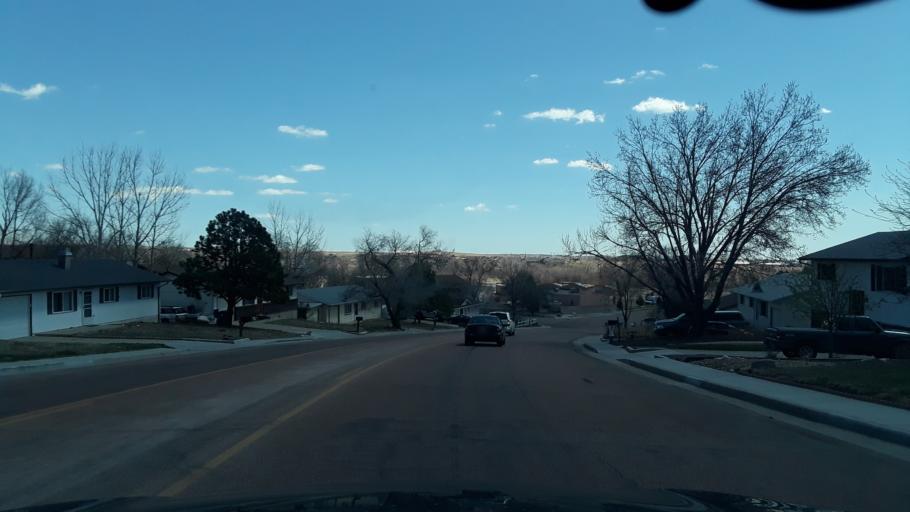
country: US
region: Colorado
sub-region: El Paso County
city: Cimarron Hills
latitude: 38.8462
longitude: -104.7046
